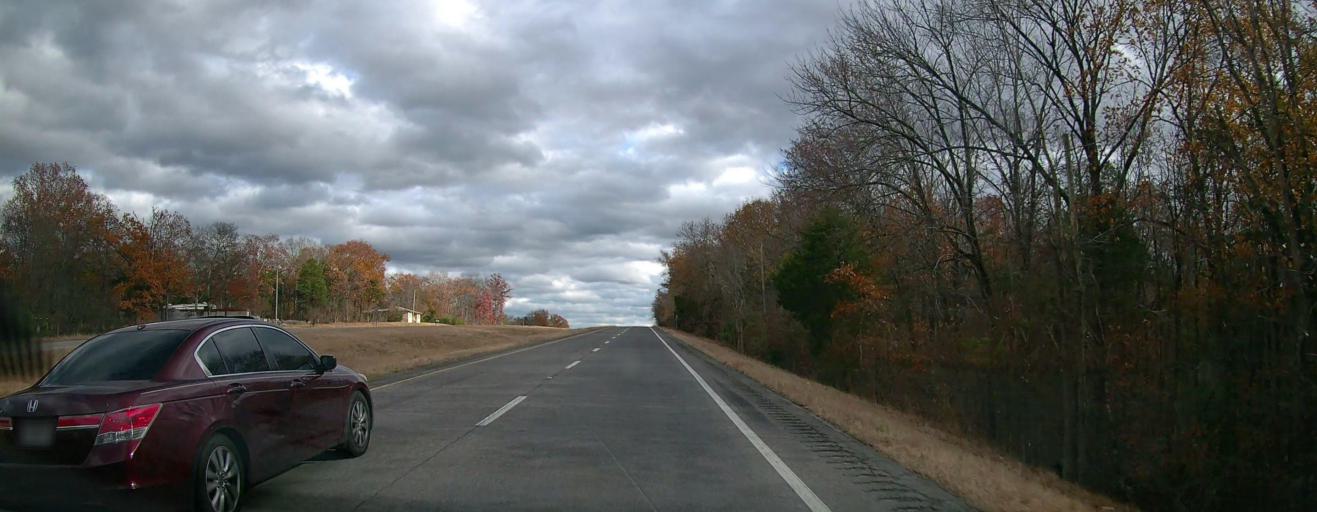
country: US
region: Alabama
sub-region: Morgan County
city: Danville
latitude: 34.3991
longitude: -87.1294
